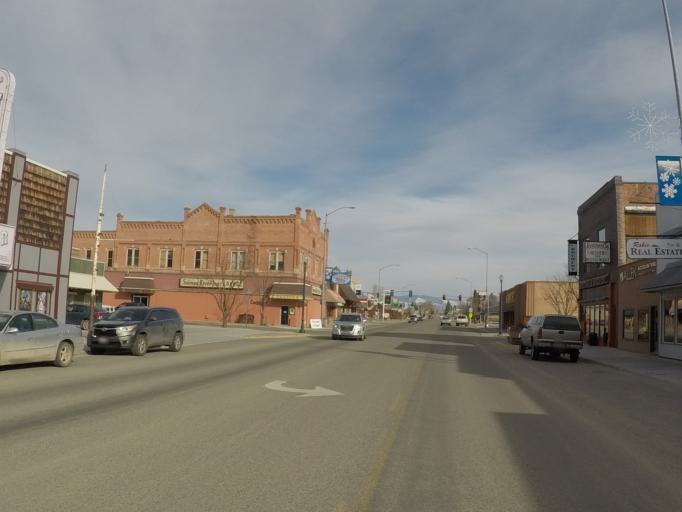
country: US
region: Idaho
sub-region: Lemhi County
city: Salmon
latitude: 45.1755
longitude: -113.8936
